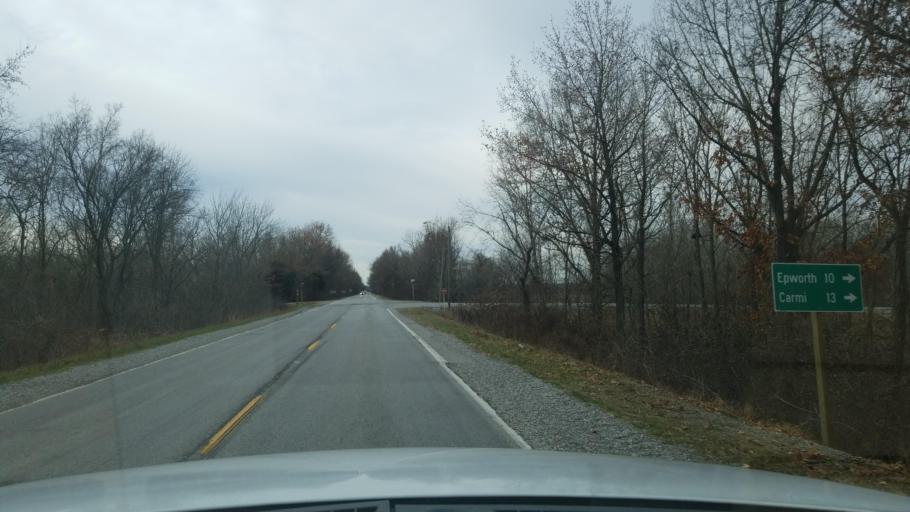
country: US
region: Illinois
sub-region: White County
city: Carmi
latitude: 37.9228
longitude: -88.1070
